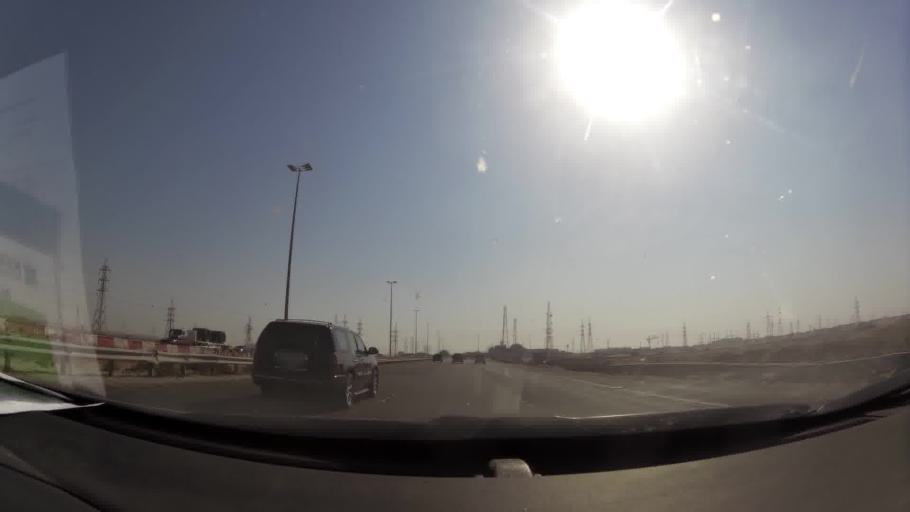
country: SA
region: Eastern Province
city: Al Khafji
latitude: 28.7385
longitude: 48.2844
